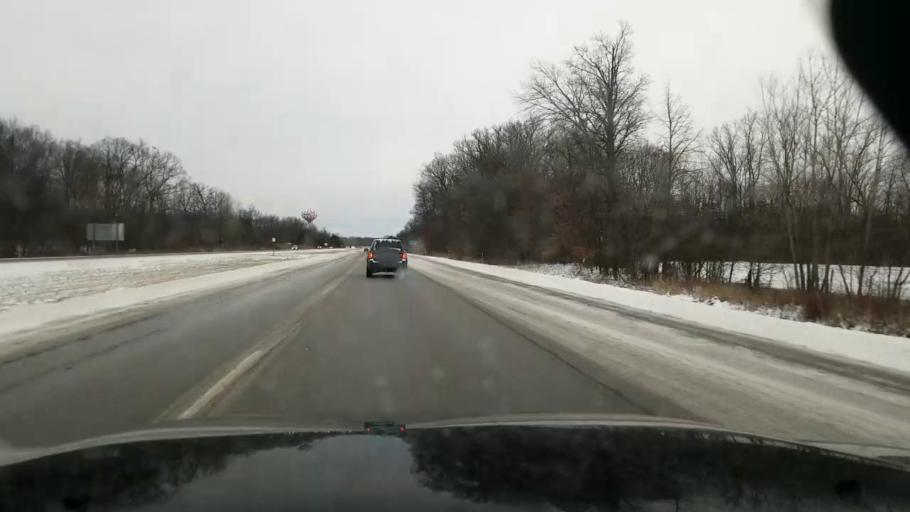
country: US
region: Michigan
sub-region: Jackson County
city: Jackson
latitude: 42.2485
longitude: -84.4761
